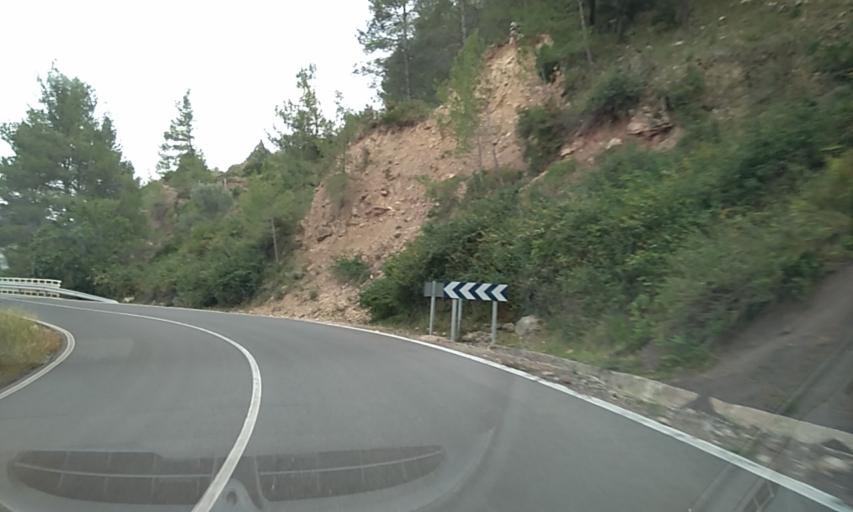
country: ES
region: Valencia
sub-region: Provincia de Castello
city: Puebla de Arenoso
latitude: 40.0851
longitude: -0.5548
